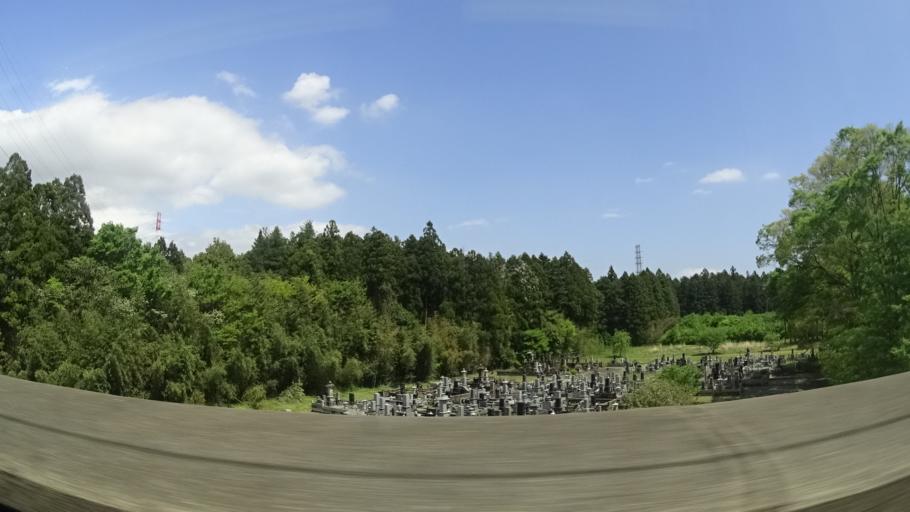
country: JP
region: Tochigi
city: Yaita
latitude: 36.8350
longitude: 139.9620
